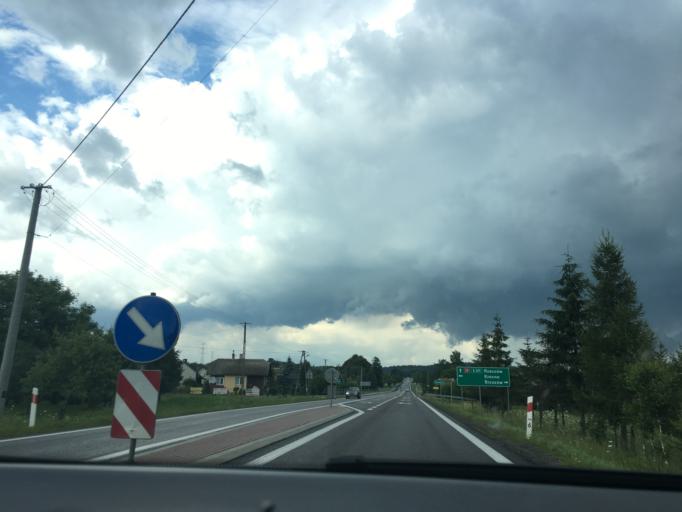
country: PL
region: Subcarpathian Voivodeship
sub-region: Powiat brzozowski
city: Jablonica Polska
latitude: 49.6991
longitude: 21.8792
